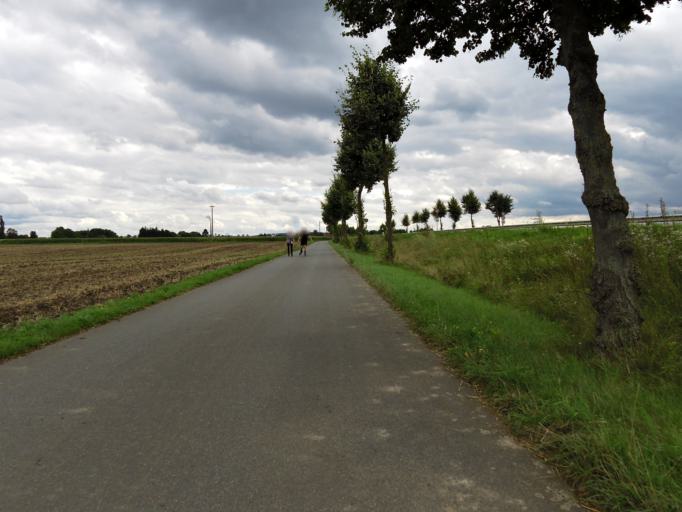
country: DE
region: Hesse
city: Lampertheim
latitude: 49.5705
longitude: 8.4481
